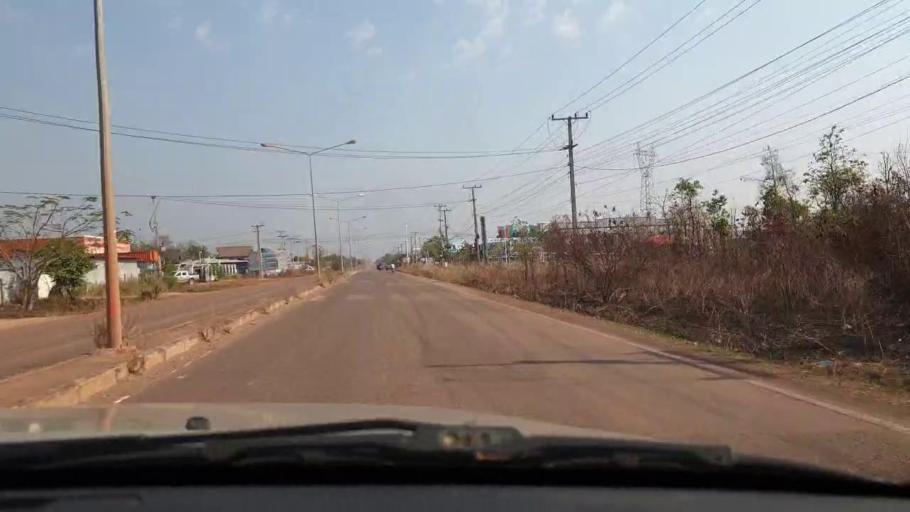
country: LA
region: Vientiane
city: Vientiane
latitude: 18.0084
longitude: 102.7211
